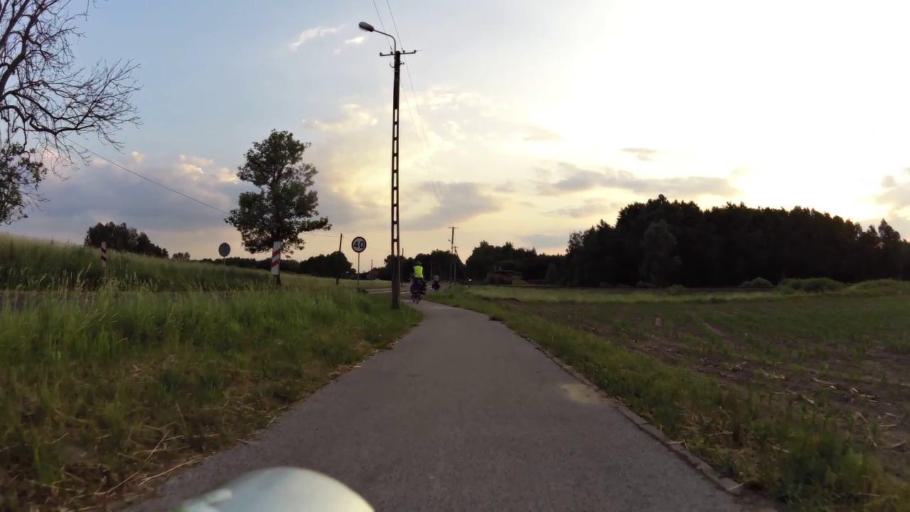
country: PL
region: Kujawsko-Pomorskie
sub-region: Powiat bydgoski
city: Dabrowa Chelminska
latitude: 53.1789
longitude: 18.2894
